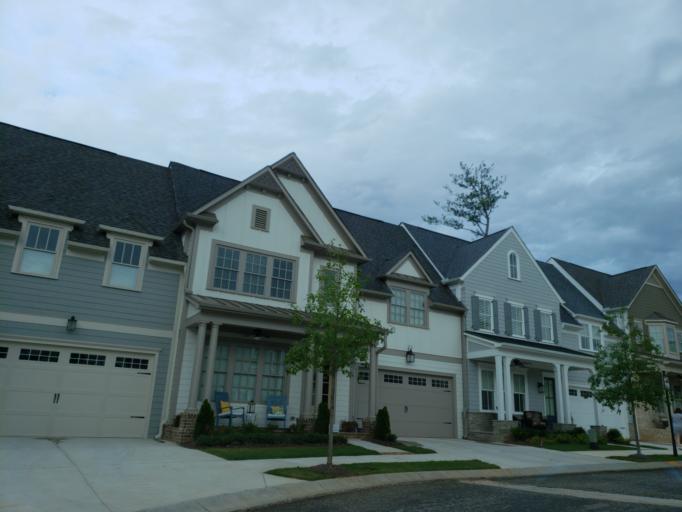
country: US
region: Georgia
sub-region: Cherokee County
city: Woodstock
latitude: 34.0934
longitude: -84.5227
